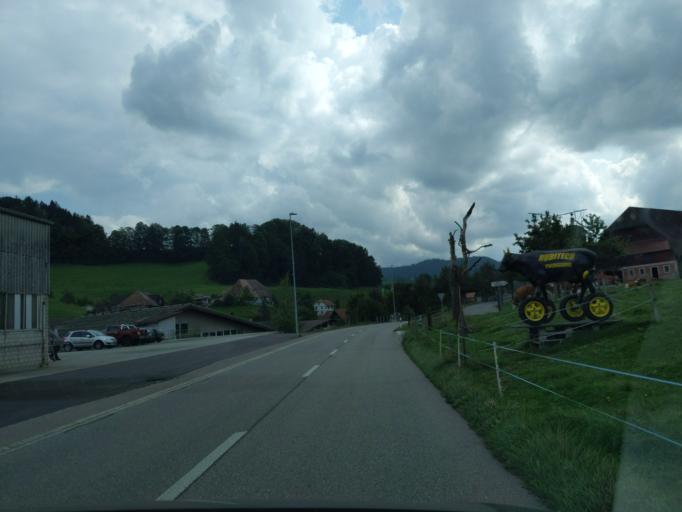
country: CH
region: Bern
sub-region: Oberaargau
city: Wyssachen
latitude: 47.0864
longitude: 7.8246
